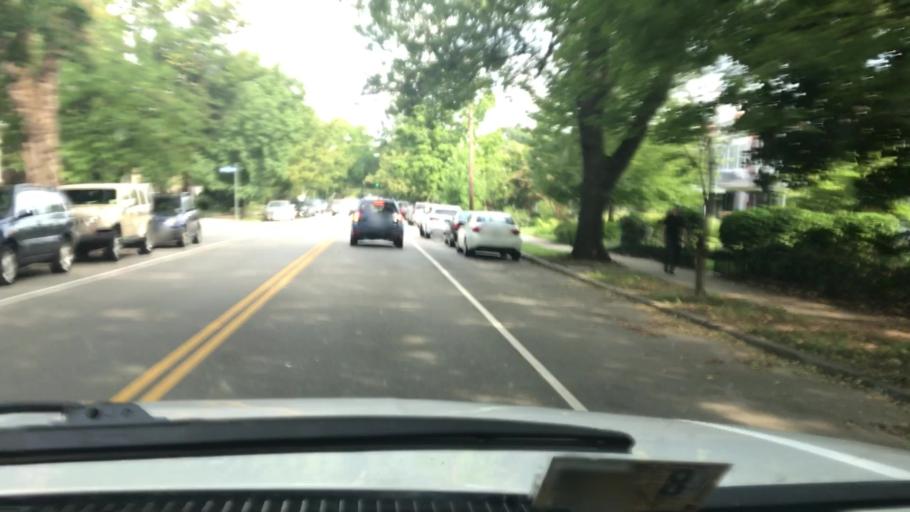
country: US
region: Virginia
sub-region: City of Richmond
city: Richmond
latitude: 37.5569
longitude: -77.4800
